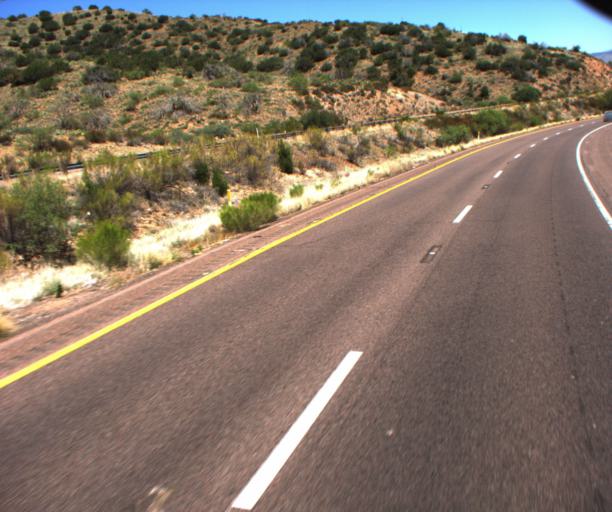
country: US
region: Arizona
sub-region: Gila County
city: Tonto Basin
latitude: 34.0125
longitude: -111.3596
